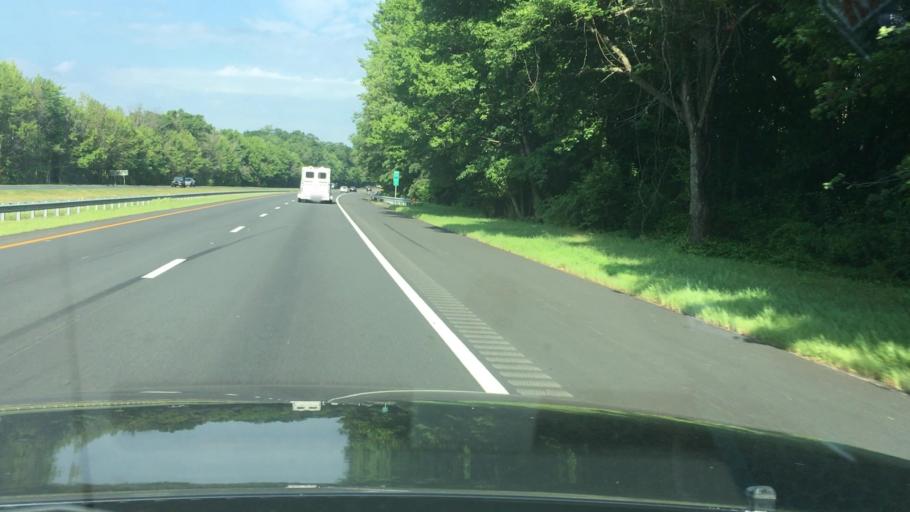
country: US
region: New Jersey
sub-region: Monmouth County
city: Shrewsbury
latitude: 40.1770
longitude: -74.5256
